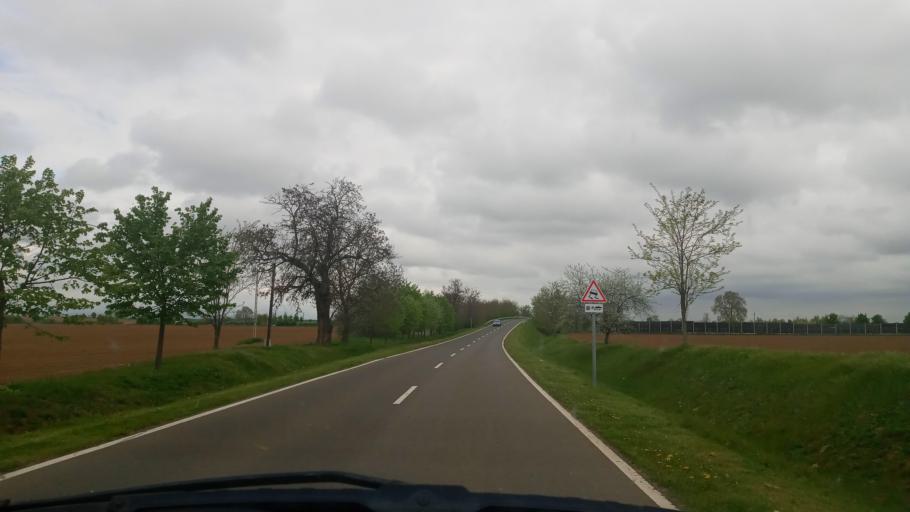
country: HU
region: Baranya
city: Kozarmisleny
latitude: 46.0079
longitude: 18.3742
